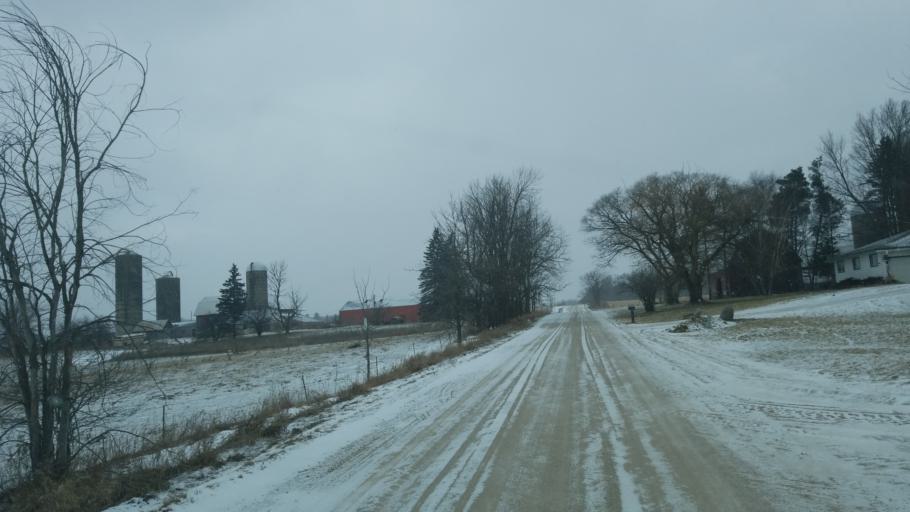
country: US
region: Michigan
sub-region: Osceola County
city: Evart
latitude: 44.0231
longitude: -85.2066
